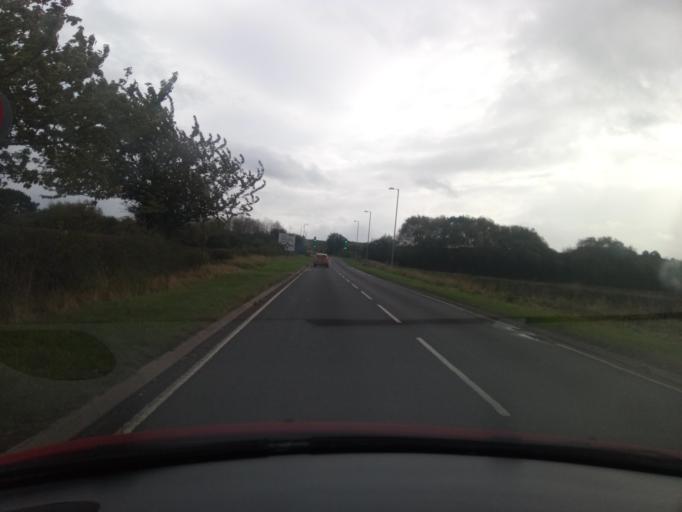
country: GB
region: England
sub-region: Nottinghamshire
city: Cotgrave
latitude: 52.9201
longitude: -1.0137
